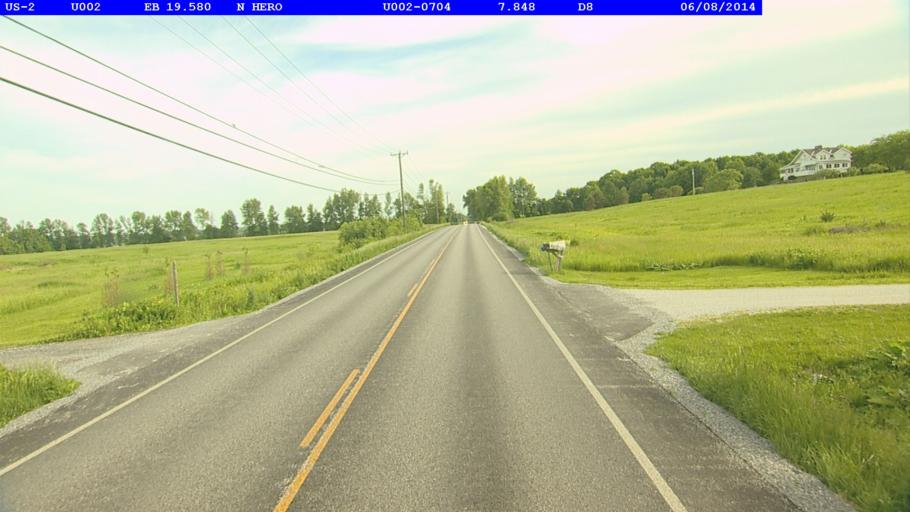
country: US
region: Vermont
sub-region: Grand Isle County
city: North Hero
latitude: 44.7867
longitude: -73.2931
